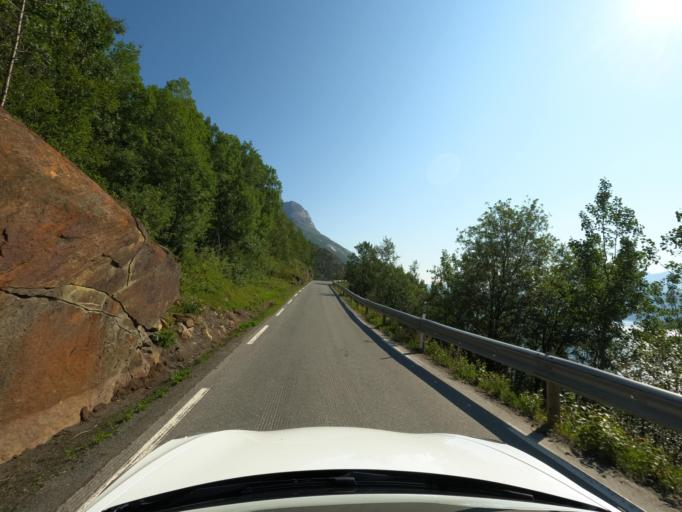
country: NO
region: Nordland
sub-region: Narvik
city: Narvik
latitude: 68.3680
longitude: 17.2534
